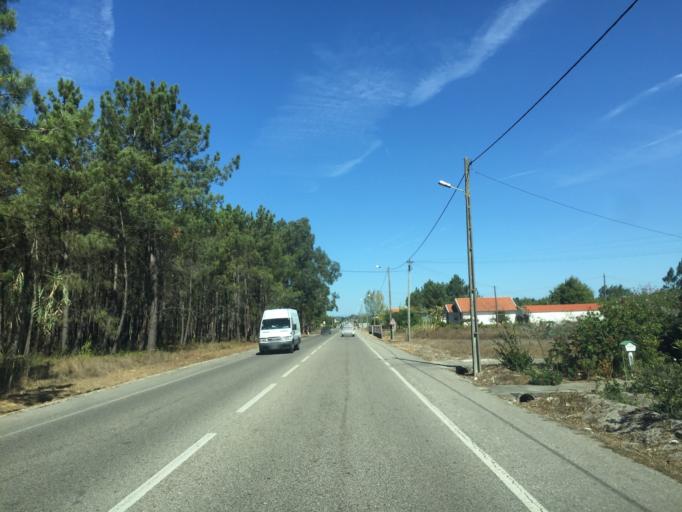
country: PT
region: Coimbra
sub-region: Figueira da Foz
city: Alhadas
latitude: 40.2237
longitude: -8.8054
